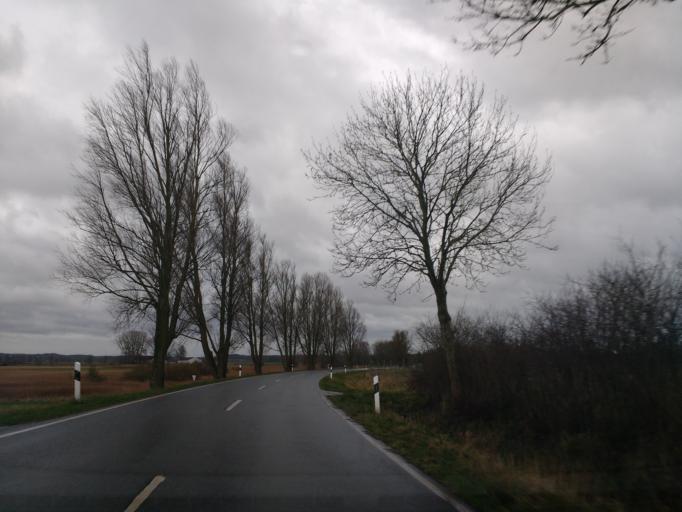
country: DE
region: Schleswig-Holstein
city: Blekendorf
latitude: 54.3123
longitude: 10.6571
